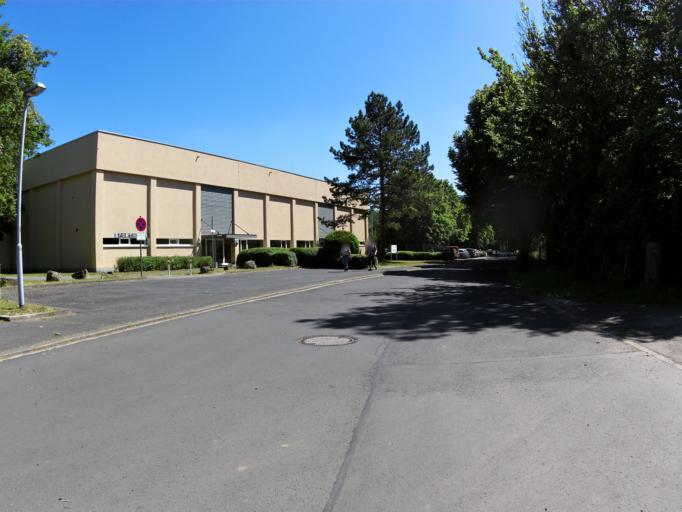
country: DE
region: Thuringia
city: Dankmarshausen
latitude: 50.9476
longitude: 10.0220
